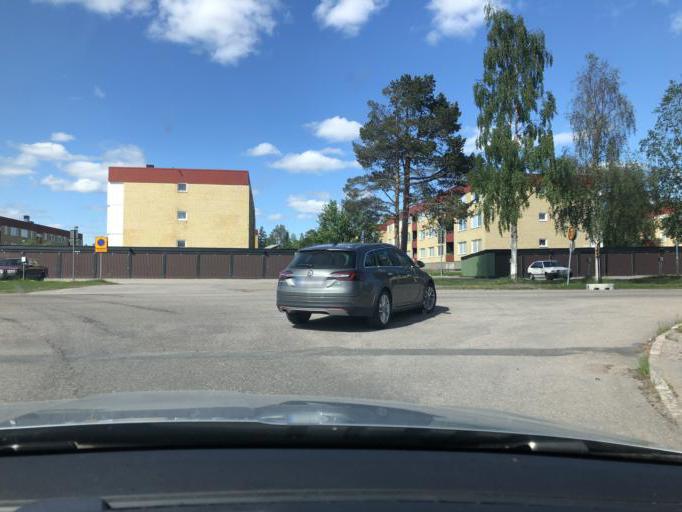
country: SE
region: Norrbotten
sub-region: Gallivare Kommun
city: Gaellivare
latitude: 67.1336
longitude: 20.6818
